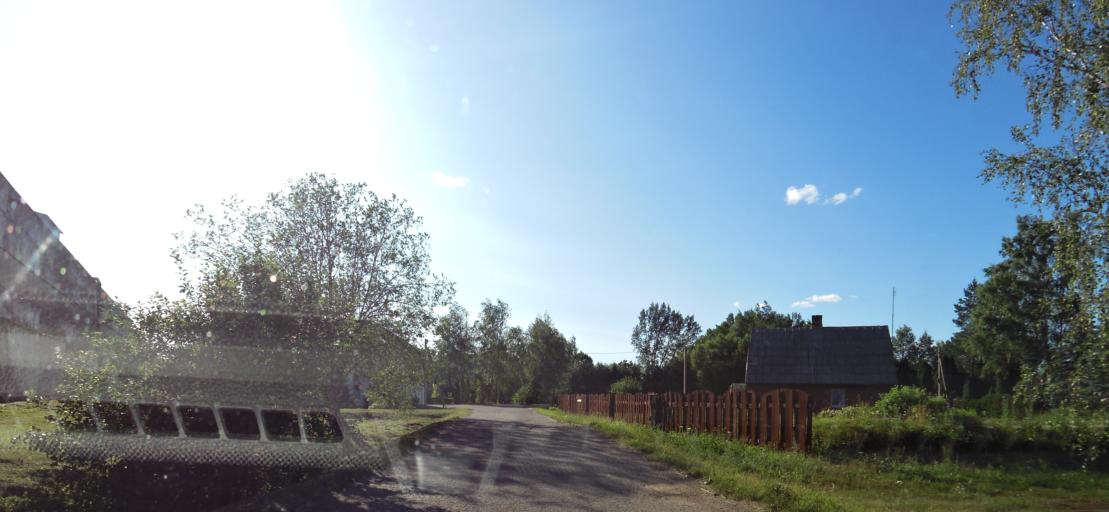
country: LT
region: Panevezys
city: Pasvalys
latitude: 56.1315
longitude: 24.5436
